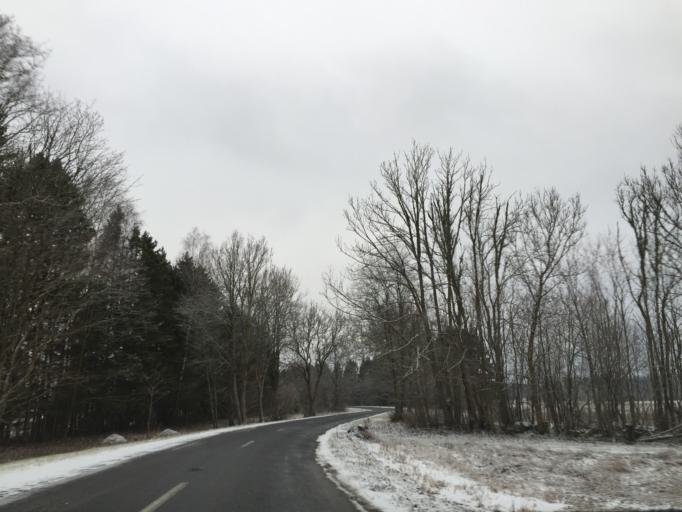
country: EE
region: Saare
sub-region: Orissaare vald
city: Orissaare
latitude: 58.6073
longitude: 23.3102
